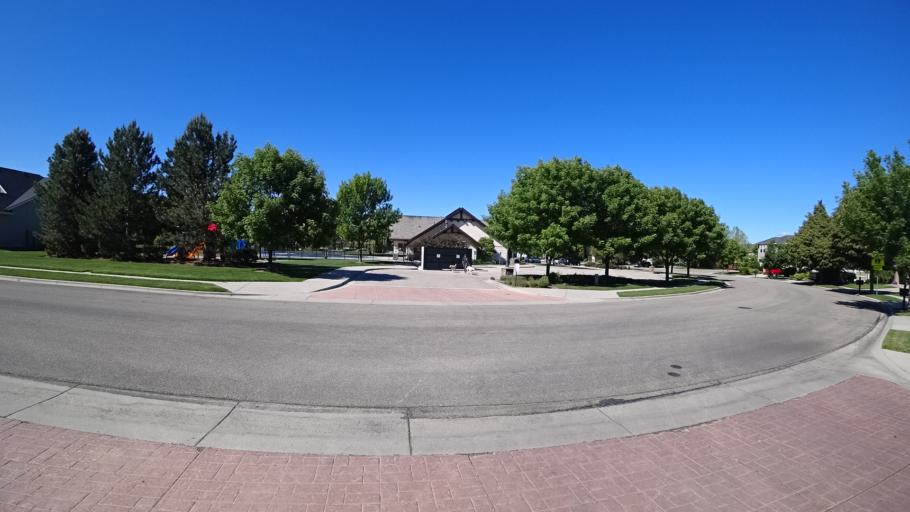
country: US
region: Idaho
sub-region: Ada County
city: Meridian
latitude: 43.6567
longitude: -116.4037
